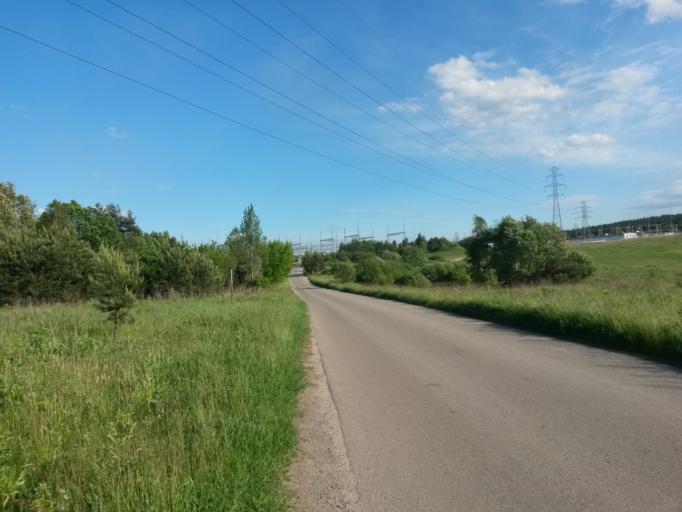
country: PL
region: Silesian Voivodeship
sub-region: Powiat zawiercianski
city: Chruszczobrod
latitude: 50.3813
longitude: 19.3290
